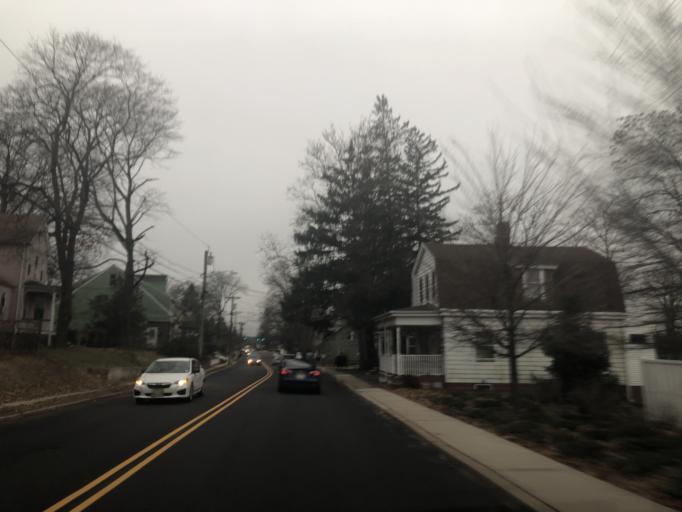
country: US
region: New Jersey
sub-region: Essex County
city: Maplewood
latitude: 40.7216
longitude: -74.2845
